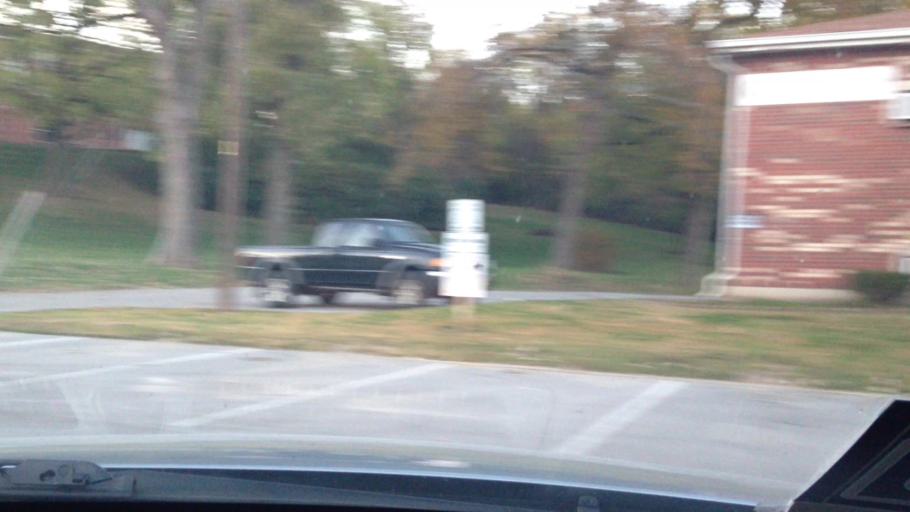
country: US
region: Missouri
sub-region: Platte County
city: Riverside
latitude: 39.1780
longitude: -94.6162
